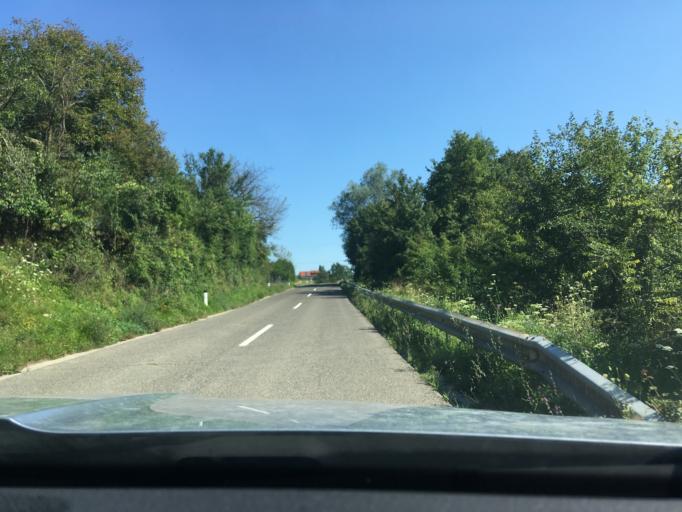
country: SI
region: Metlika
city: Metlika
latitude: 45.5185
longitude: 15.3171
